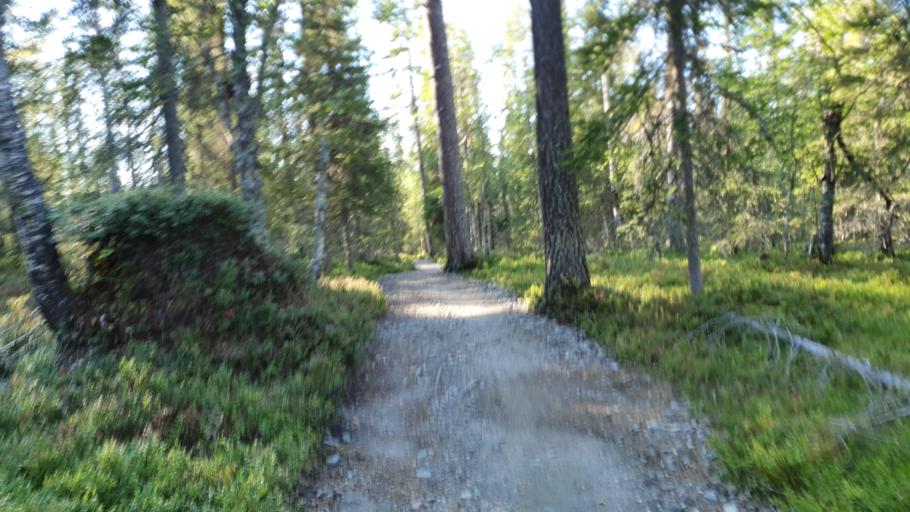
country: FI
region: Lapland
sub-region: Tunturi-Lappi
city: Kolari
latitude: 67.5980
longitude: 24.2157
